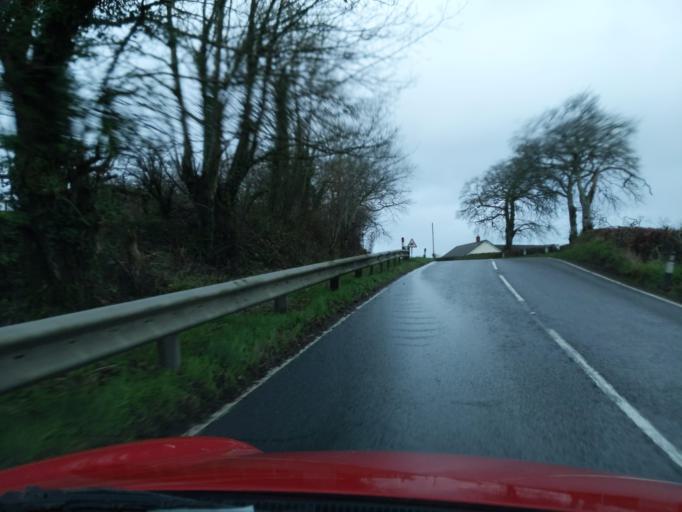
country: GB
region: England
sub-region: Devon
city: Holsworthy
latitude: 50.7573
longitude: -4.3305
